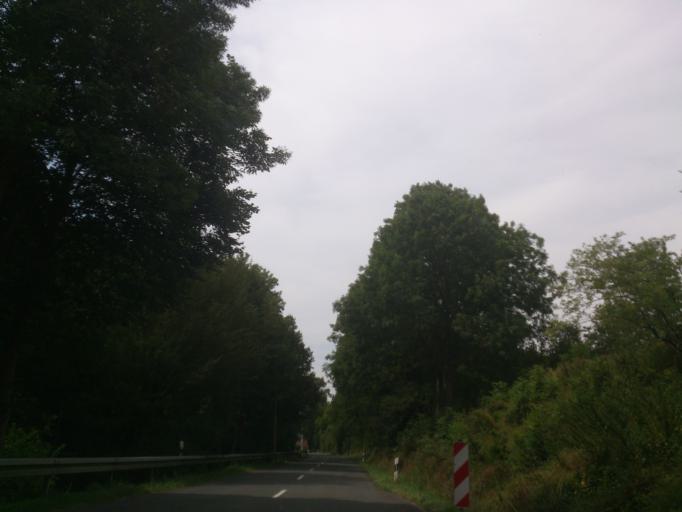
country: DE
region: North Rhine-Westphalia
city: Lichtenau
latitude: 51.5868
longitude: 8.8423
